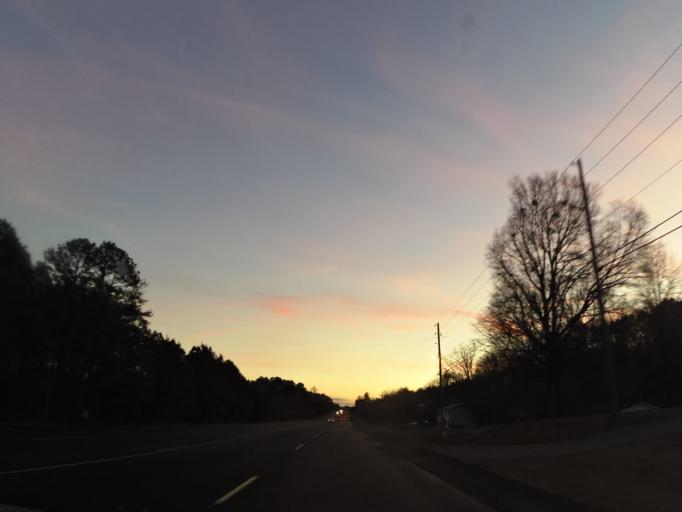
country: US
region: Georgia
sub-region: Whitfield County
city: Varnell
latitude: 34.9522
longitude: -84.9399
